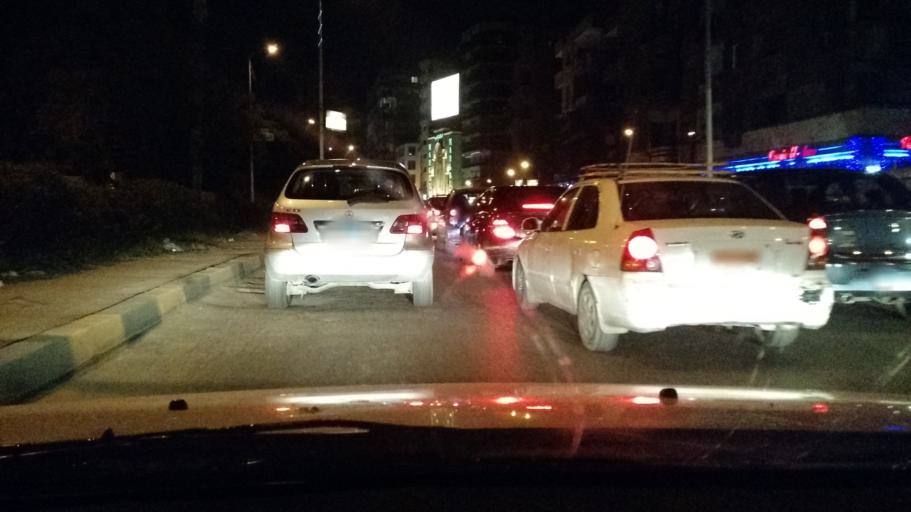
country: EG
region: Al Jizah
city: Al Jizah
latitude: 30.0145
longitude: 31.2171
